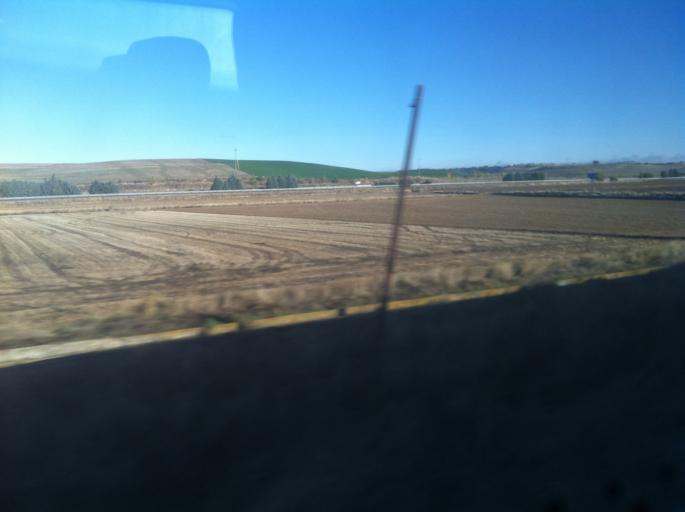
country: ES
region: Castille and Leon
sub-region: Provincia de Palencia
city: Reinoso de Cerrato
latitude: 41.9939
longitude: -4.3882
